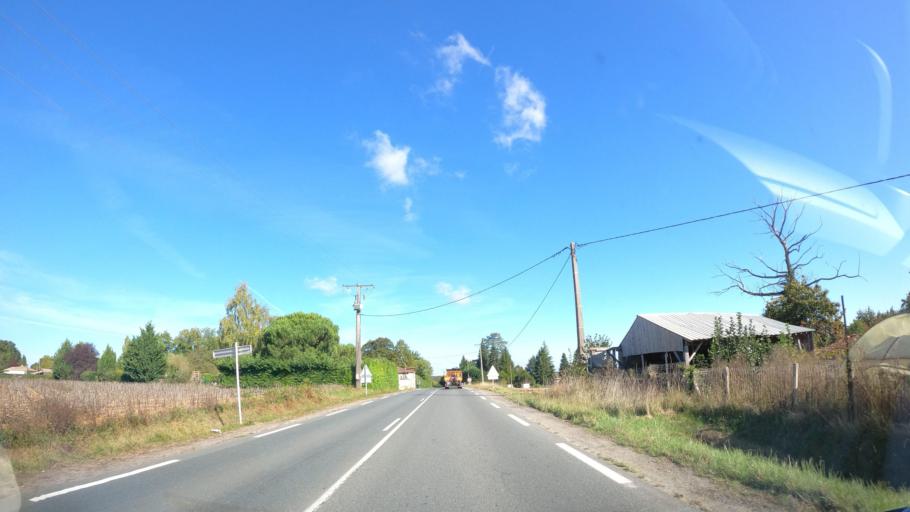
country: FR
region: Aquitaine
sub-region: Departement de la Dordogne
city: Notre-Dame-de-Sanilhac
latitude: 45.1179
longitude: 0.6950
